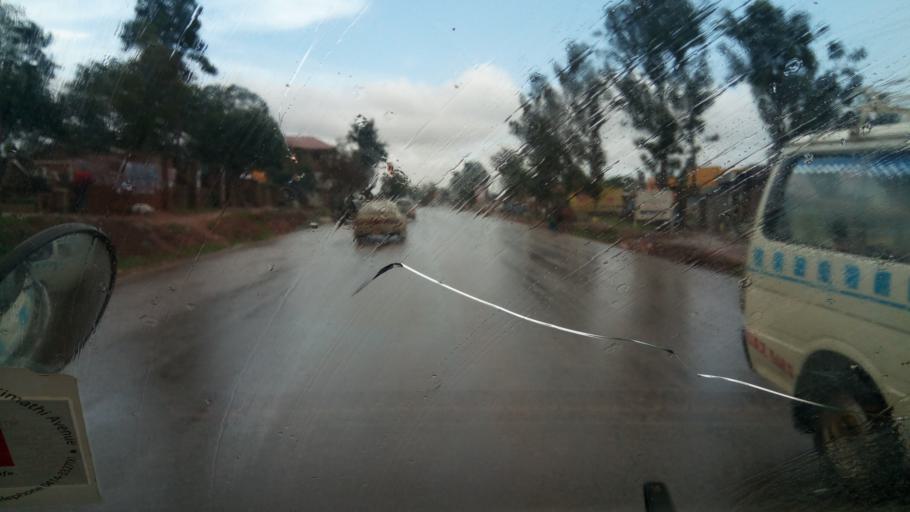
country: UG
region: Central Region
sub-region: Wakiso District
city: Wakiso
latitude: 0.3853
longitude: 32.5156
